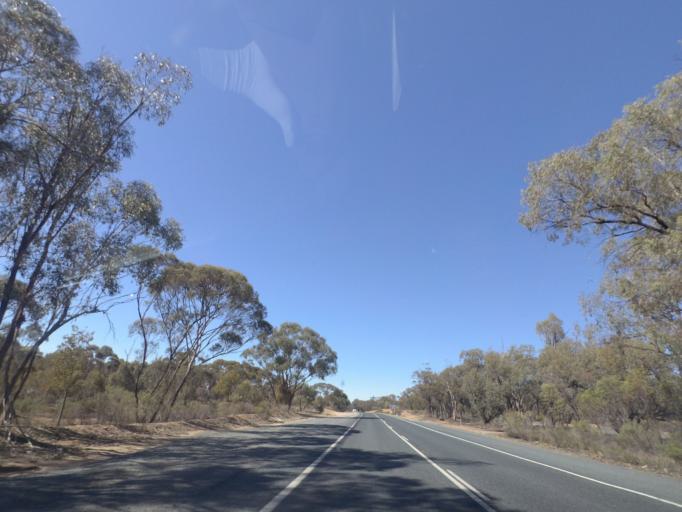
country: AU
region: New South Wales
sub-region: Bland
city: West Wyalong
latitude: -34.1370
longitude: 147.1213
